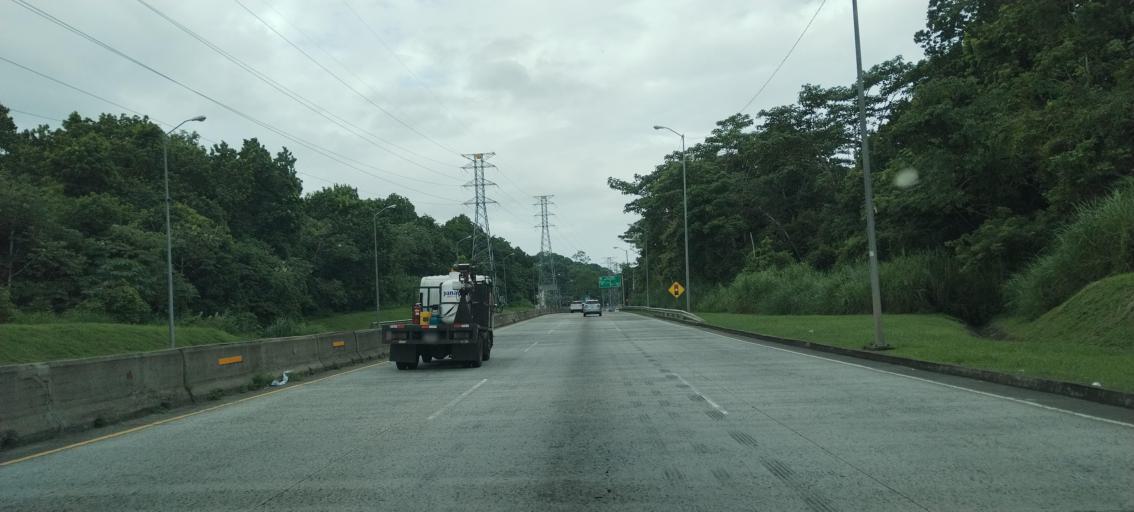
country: PA
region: Panama
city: San Miguelito
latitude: 9.0731
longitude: -79.4625
